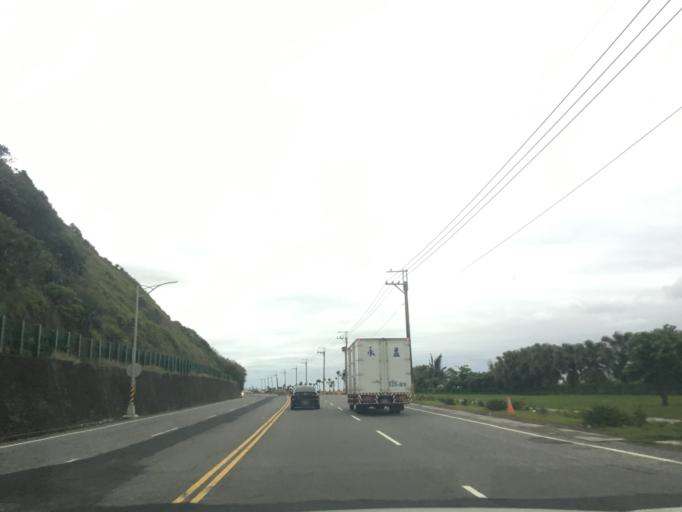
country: TW
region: Taiwan
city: Hengchun
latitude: 22.3441
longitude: 120.8979
